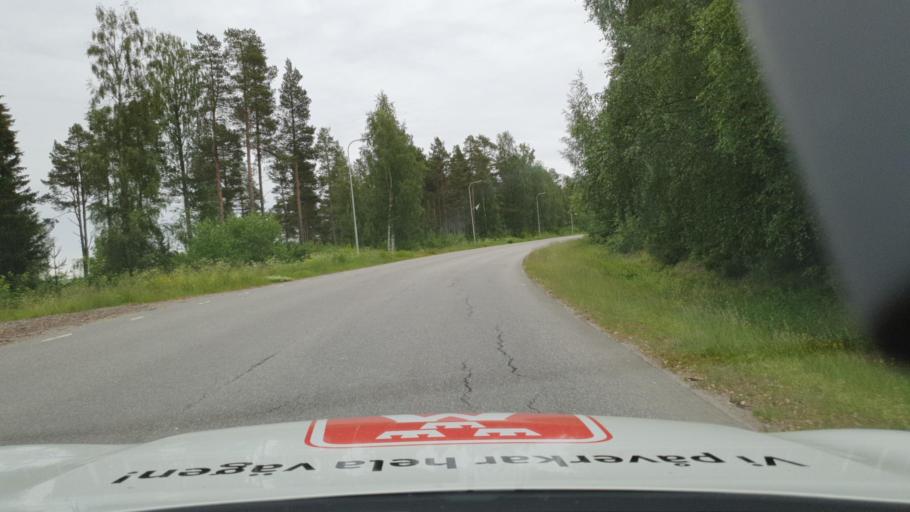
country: SE
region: Vaesterbotten
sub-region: Nordmalings Kommun
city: Nordmaling
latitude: 63.5461
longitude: 19.4366
